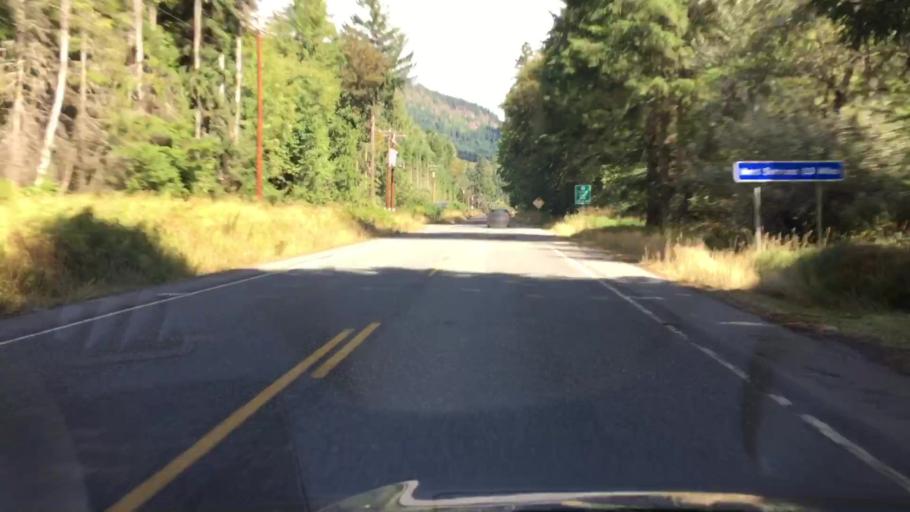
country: US
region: Washington
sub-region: Pierce County
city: Eatonville
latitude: 46.7590
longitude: -122.0462
